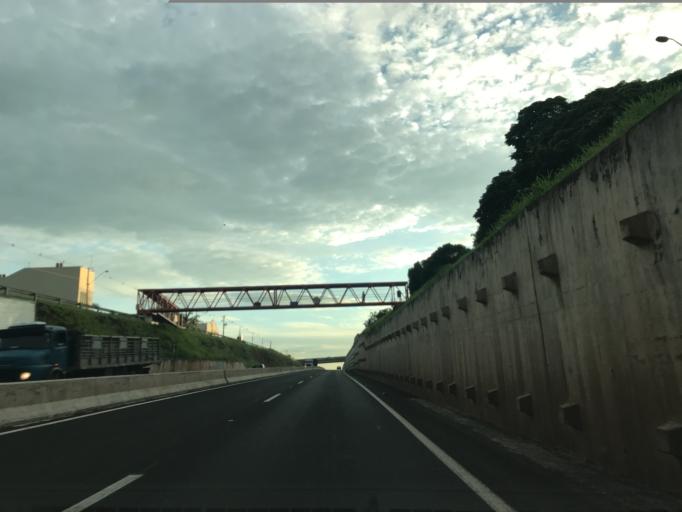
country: BR
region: Parana
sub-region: Maringa
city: Maringa
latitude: -23.3783
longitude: -51.9449
